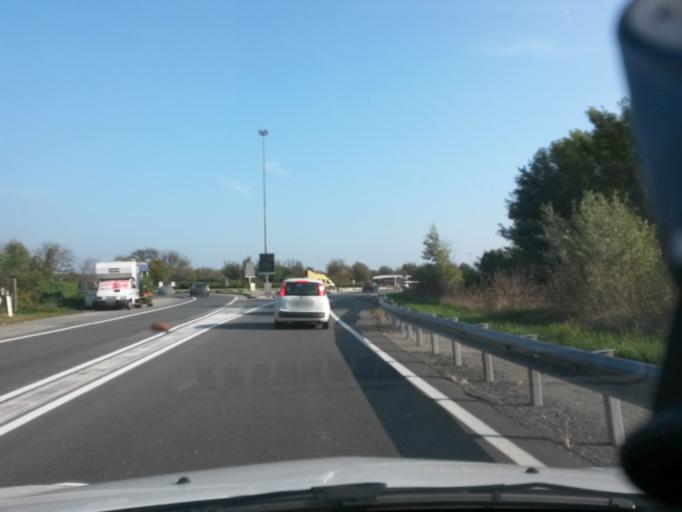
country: IT
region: Piedmont
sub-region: Provincia di Torino
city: Almese-Rivera
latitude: 45.0997
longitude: 7.3973
